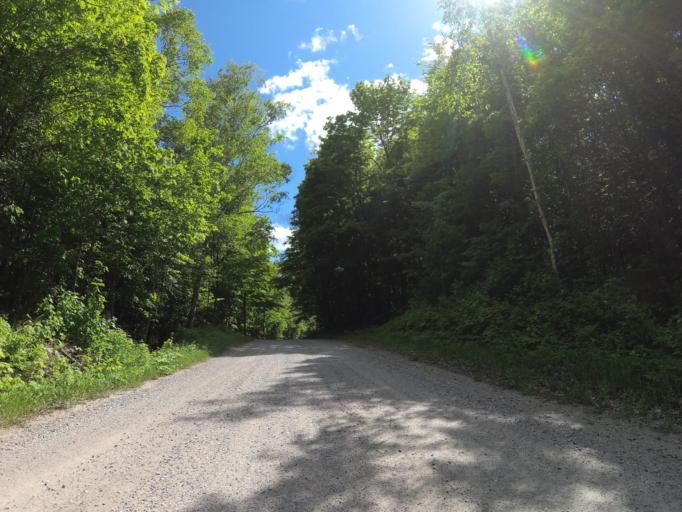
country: CA
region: Ontario
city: Renfrew
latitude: 45.0438
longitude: -76.8230
